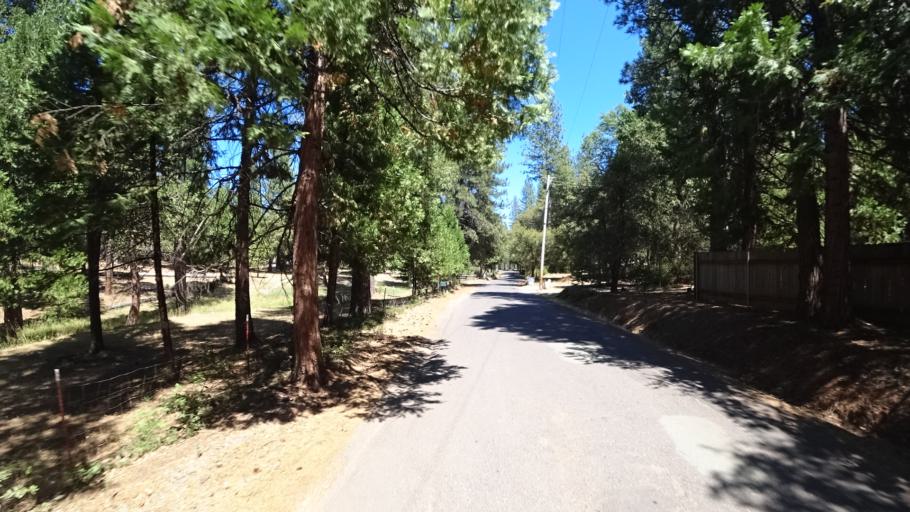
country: US
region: California
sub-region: Calaveras County
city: Mountain Ranch
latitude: 38.2813
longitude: -120.5395
